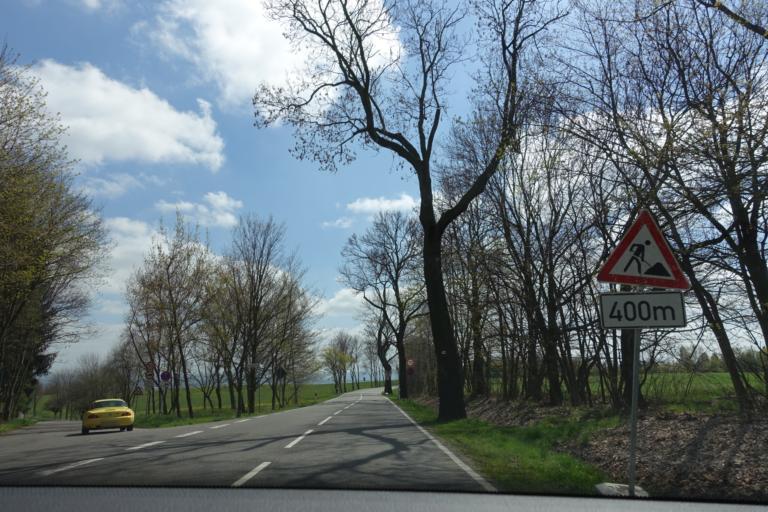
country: DE
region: Saxony
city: Limbach-Oberfrohna
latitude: 50.8395
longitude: 12.8173
